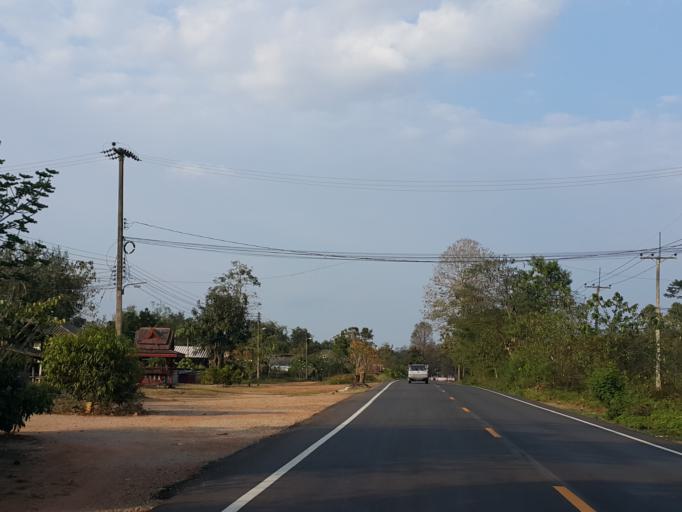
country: TH
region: Lampang
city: Lampang
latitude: 18.4810
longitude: 99.4707
